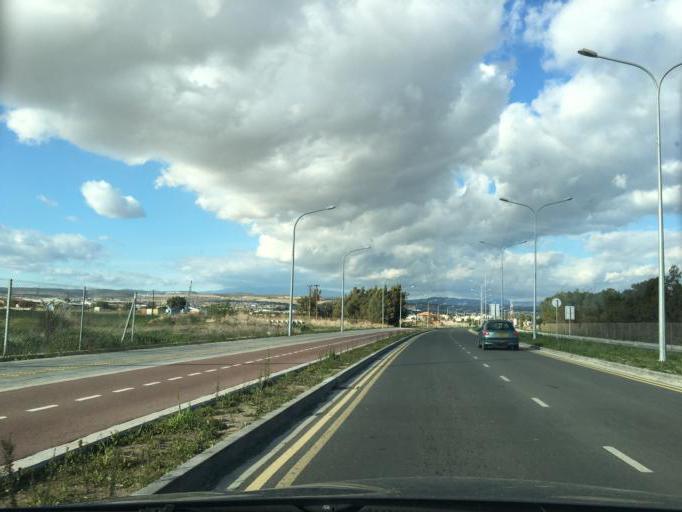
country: CY
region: Limassol
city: Ypsonas
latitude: 34.6715
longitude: 32.9888
